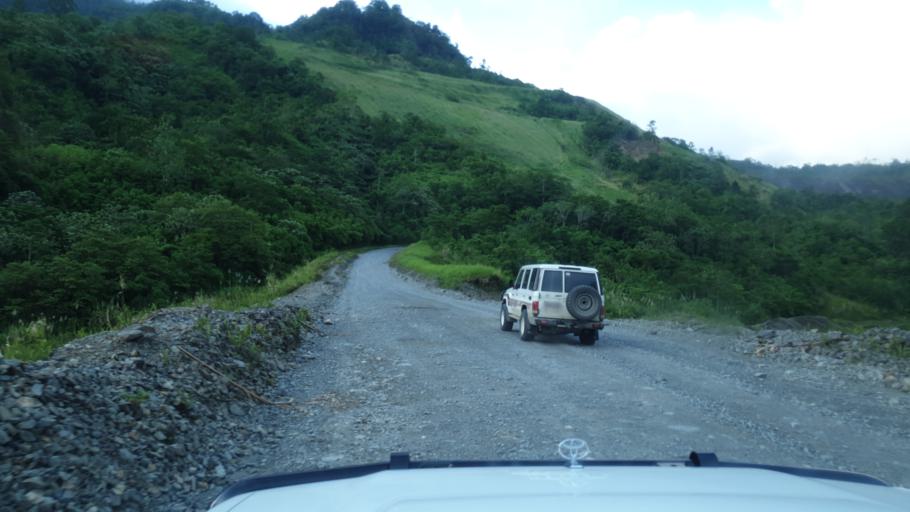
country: PG
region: Bougainville
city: Panguna
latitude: -6.3394
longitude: 155.4589
